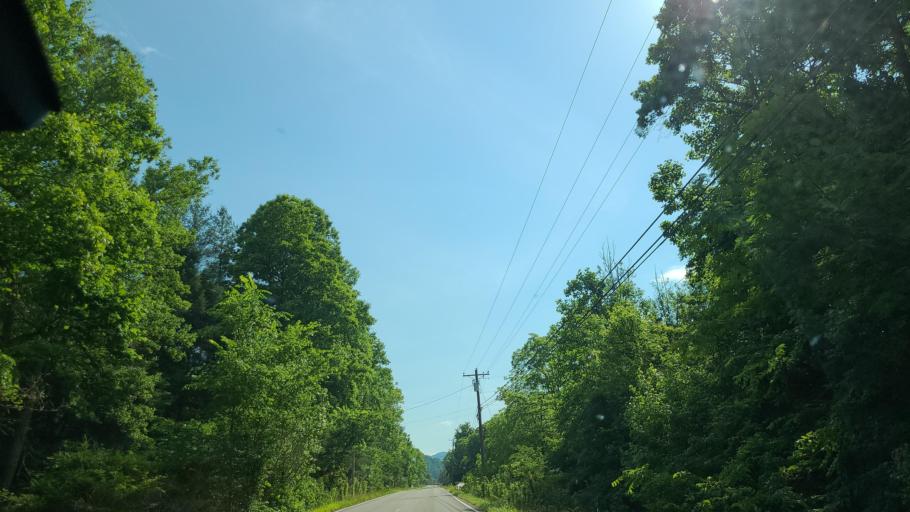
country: US
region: Kentucky
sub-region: Bell County
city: Middlesboro
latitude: 36.7012
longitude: -83.8484
